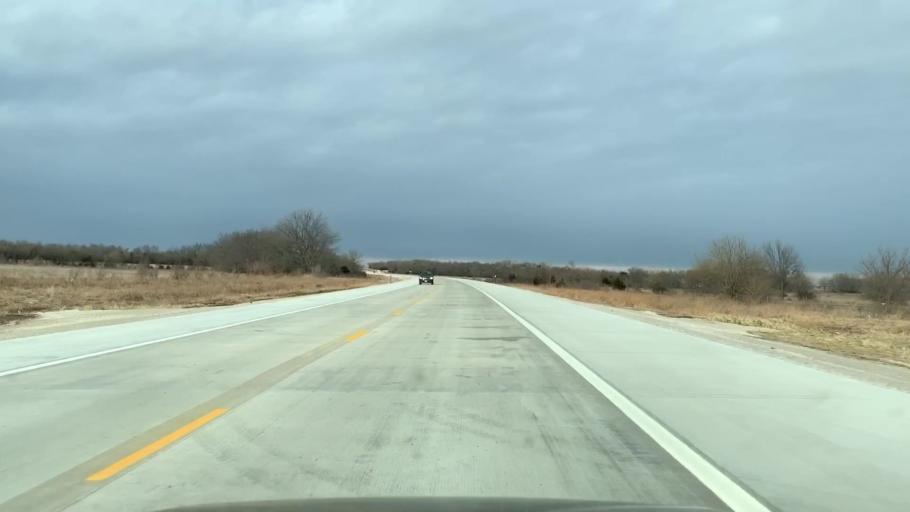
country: US
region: Kansas
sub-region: Allen County
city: Humboldt
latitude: 37.8605
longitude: -95.4053
